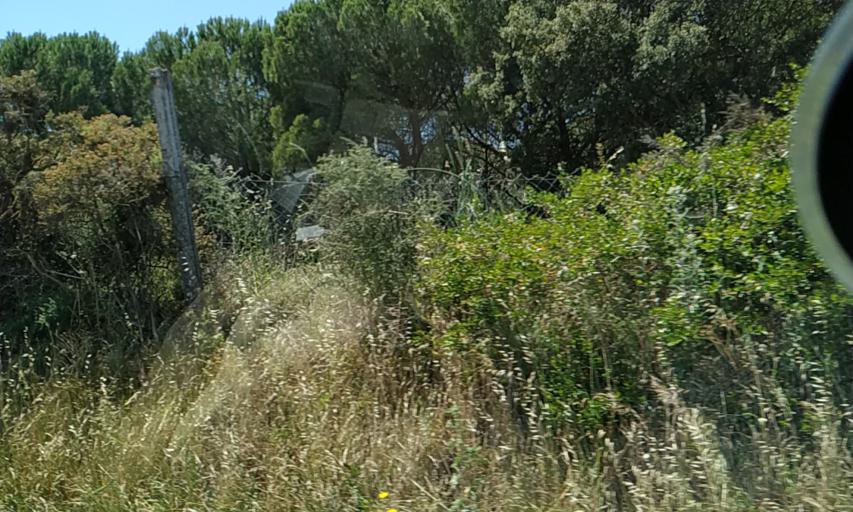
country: PT
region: Santarem
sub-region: Benavente
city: Poceirao
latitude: 38.6893
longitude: -8.7305
